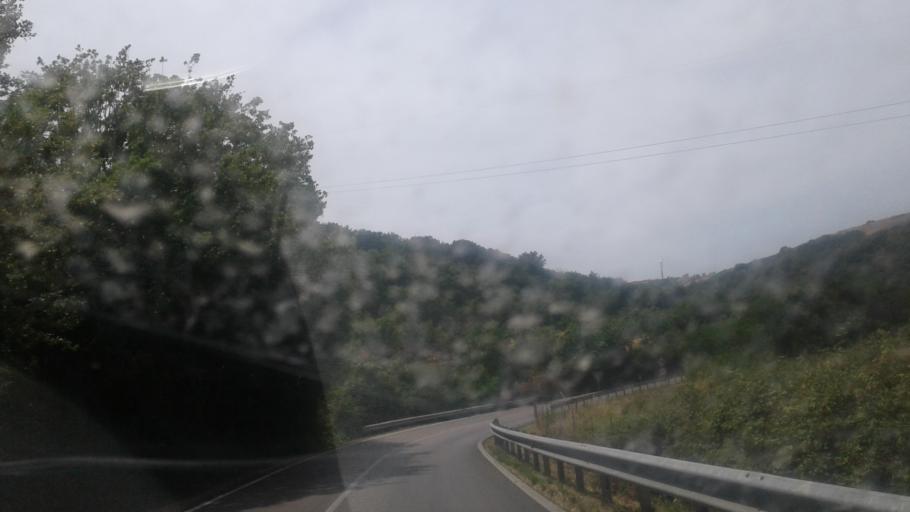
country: IT
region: Sardinia
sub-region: Provincia di Olbia-Tempio
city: Tempio Pausania
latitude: 40.9074
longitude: 9.0913
